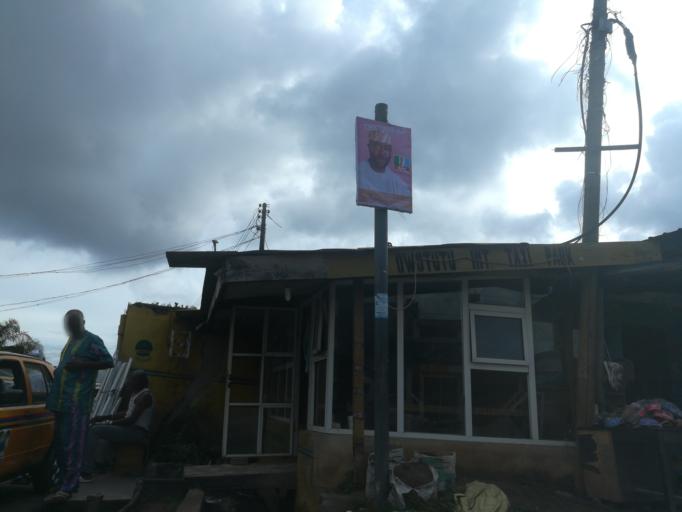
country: NG
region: Lagos
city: Somolu
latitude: 6.5406
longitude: 3.3805
